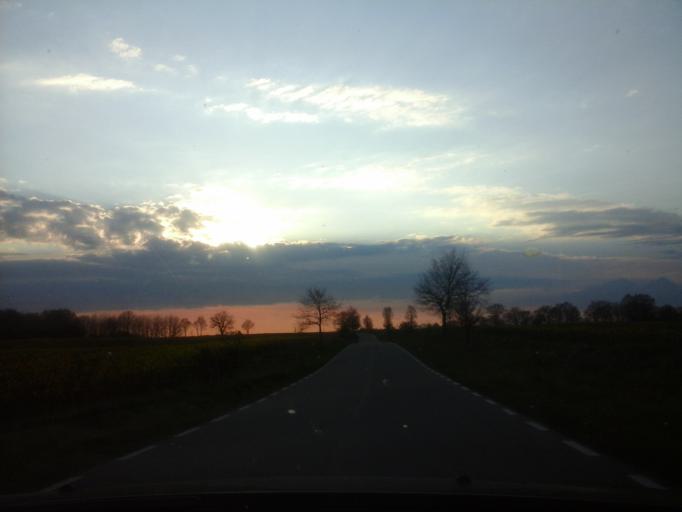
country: PL
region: West Pomeranian Voivodeship
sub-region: Powiat choszczenski
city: Pelczyce
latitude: 53.0061
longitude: 15.4004
